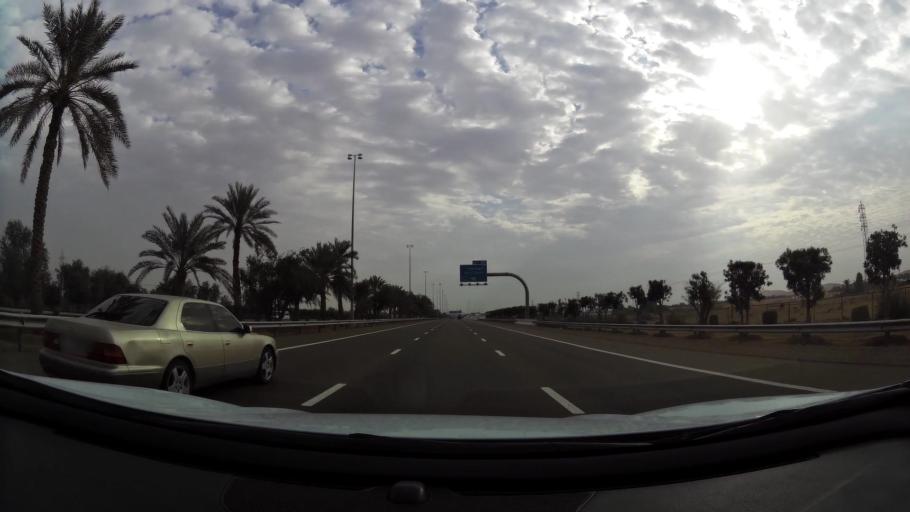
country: AE
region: Abu Dhabi
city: Al Ain
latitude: 24.2015
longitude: 55.3764
